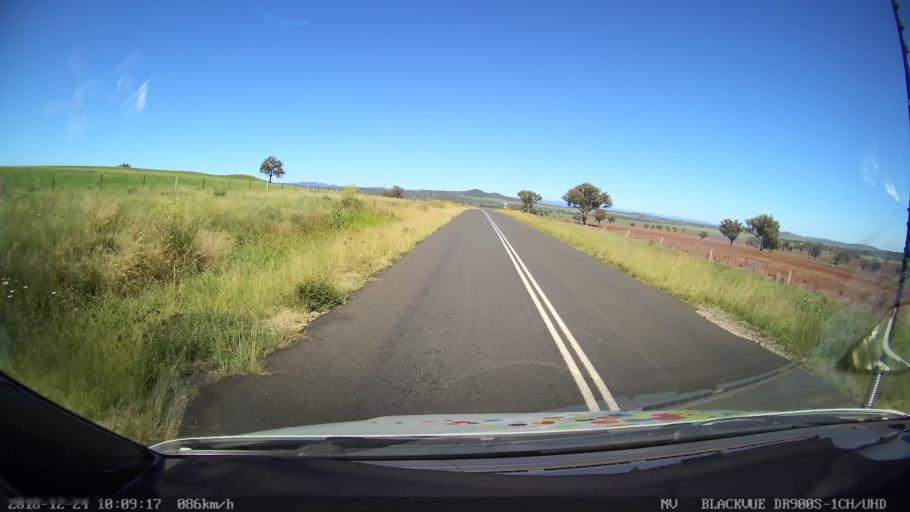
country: AU
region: New South Wales
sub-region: Liverpool Plains
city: Quirindi
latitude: -31.6628
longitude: 150.6935
